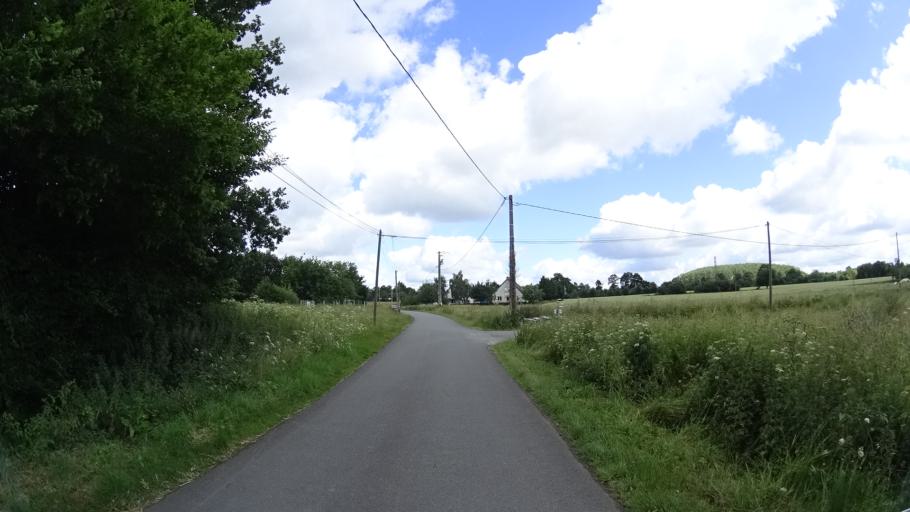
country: FR
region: Brittany
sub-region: Departement d'Ille-et-Vilaine
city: Le Rheu
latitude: 48.1139
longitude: -1.8146
